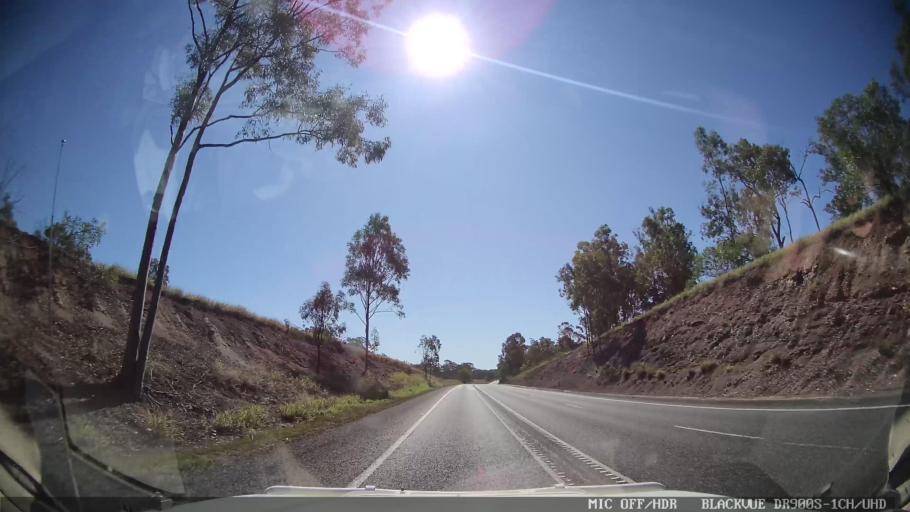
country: AU
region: Queensland
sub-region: Fraser Coast
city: Maryborough
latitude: -25.7724
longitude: 152.5966
